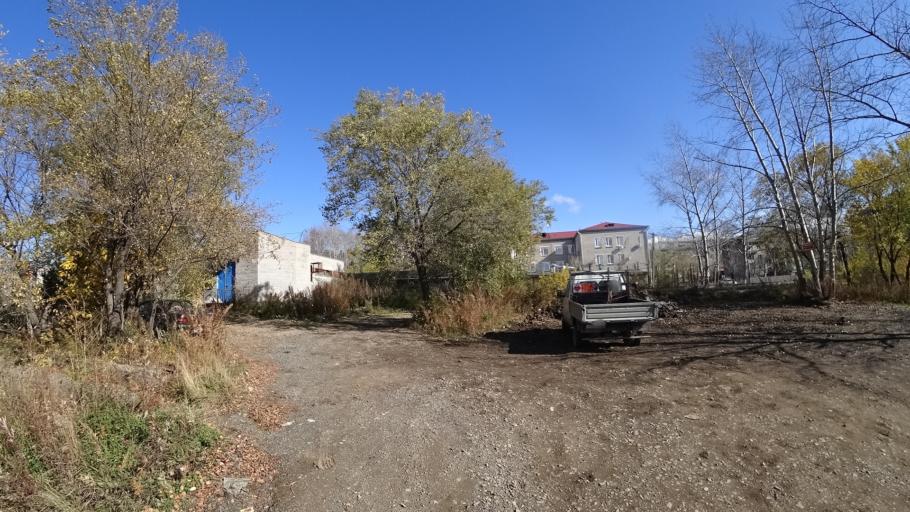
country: RU
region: Khabarovsk Krai
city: Amursk
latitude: 50.2189
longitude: 136.9013
